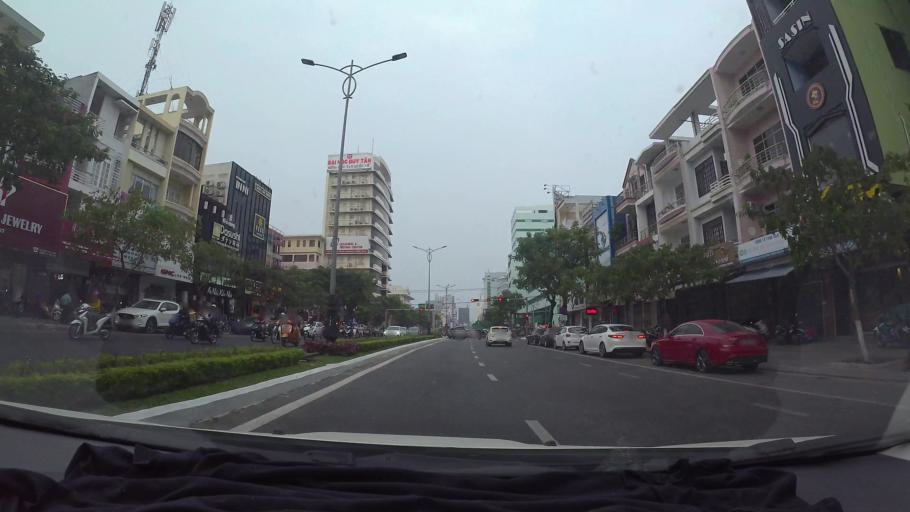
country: VN
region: Da Nang
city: Da Nang
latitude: 16.0595
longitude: 108.2087
